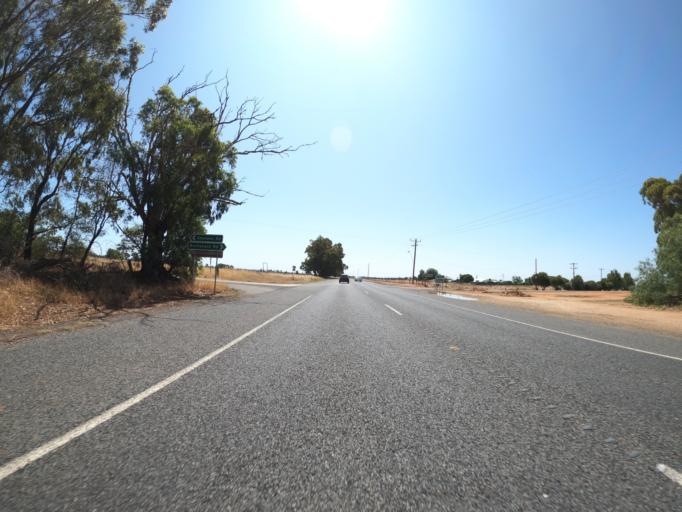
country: AU
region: Victoria
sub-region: Moira
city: Yarrawonga
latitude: -36.0255
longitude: 146.0673
